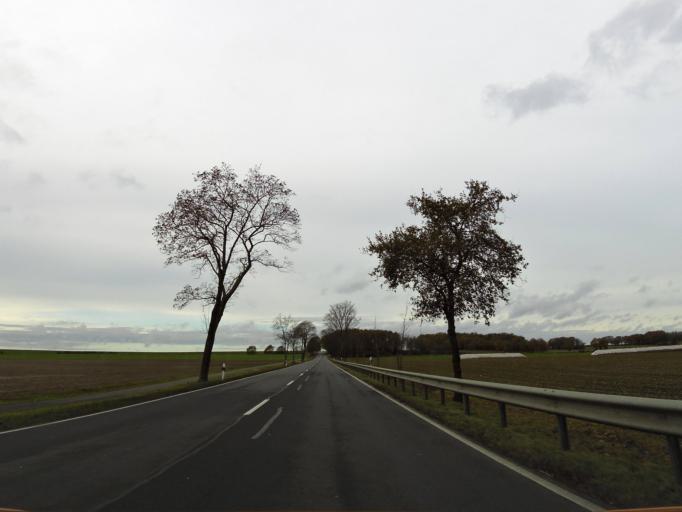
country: DE
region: Lower Saxony
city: Suhlendorf
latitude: 52.9402
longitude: 10.7431
